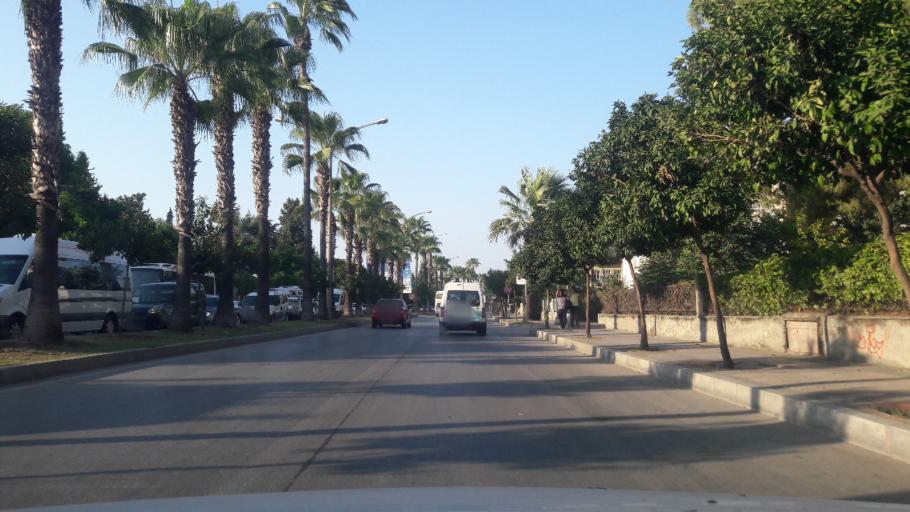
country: TR
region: Adana
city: Seyhan
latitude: 36.9879
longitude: 35.2981
